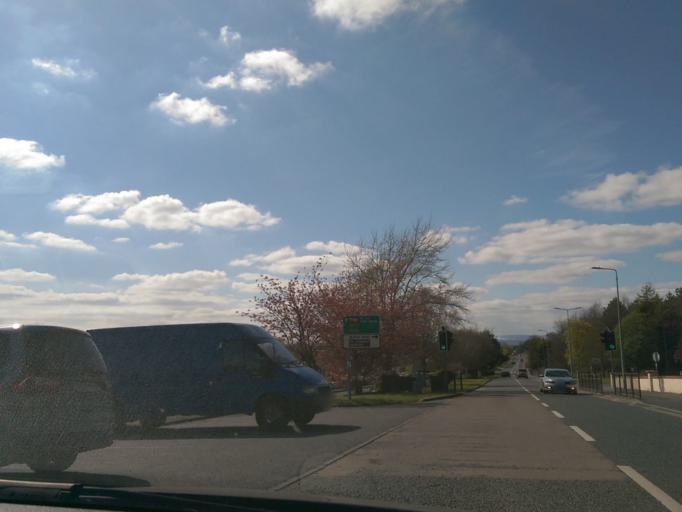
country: IE
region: Leinster
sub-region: Laois
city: Portlaoise
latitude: 53.0330
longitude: -7.2729
